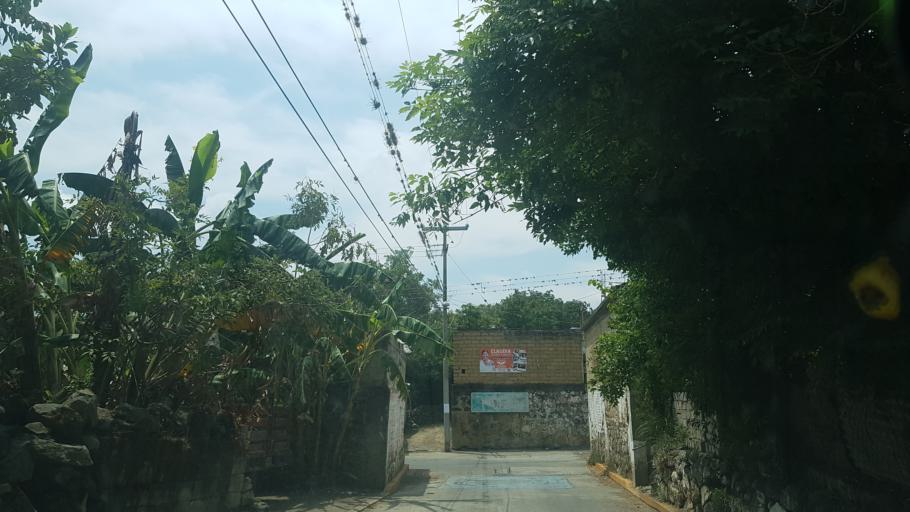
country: MX
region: Puebla
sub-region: Tochimilco
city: La Magdalena Yancuitlalpan
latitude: 18.8882
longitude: -98.6111
